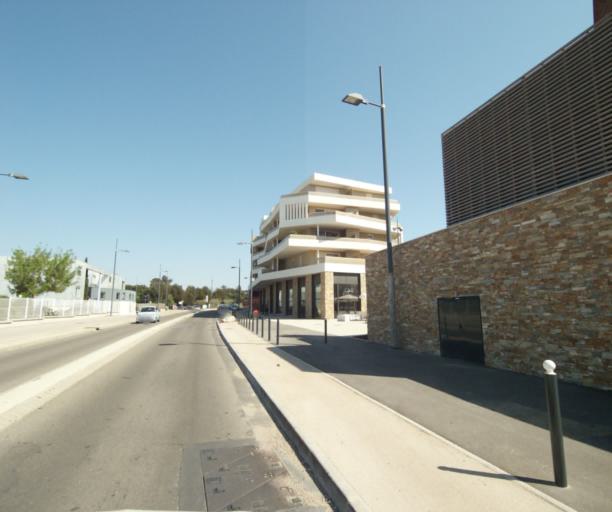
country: FR
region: Languedoc-Roussillon
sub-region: Departement de l'Herault
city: Castelnau-le-Lez
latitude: 43.6260
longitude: 3.9046
